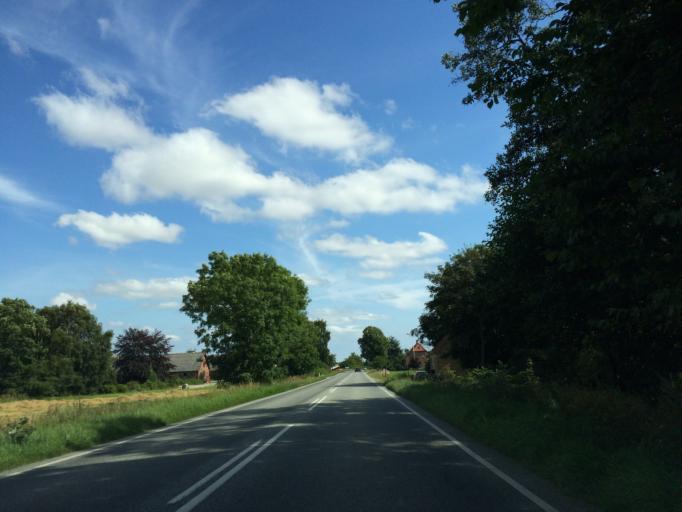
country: DK
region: Central Jutland
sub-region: Syddjurs Kommune
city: Ronde
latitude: 56.3116
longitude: 10.4381
